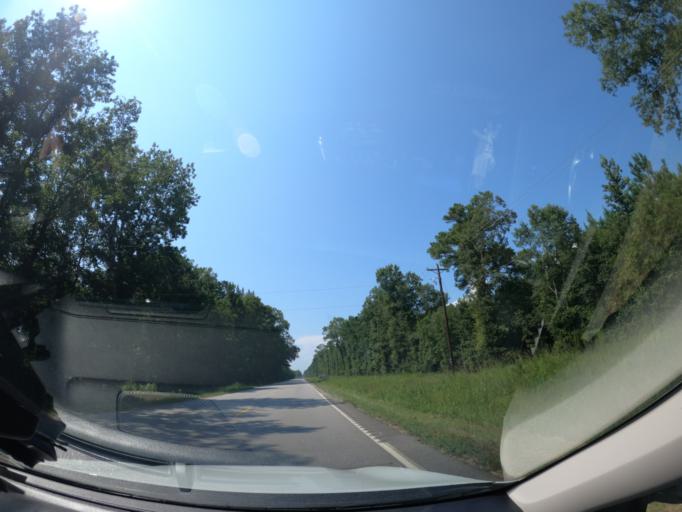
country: US
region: South Carolina
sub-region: Richland County
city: Hopkins
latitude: 33.8751
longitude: -80.8991
